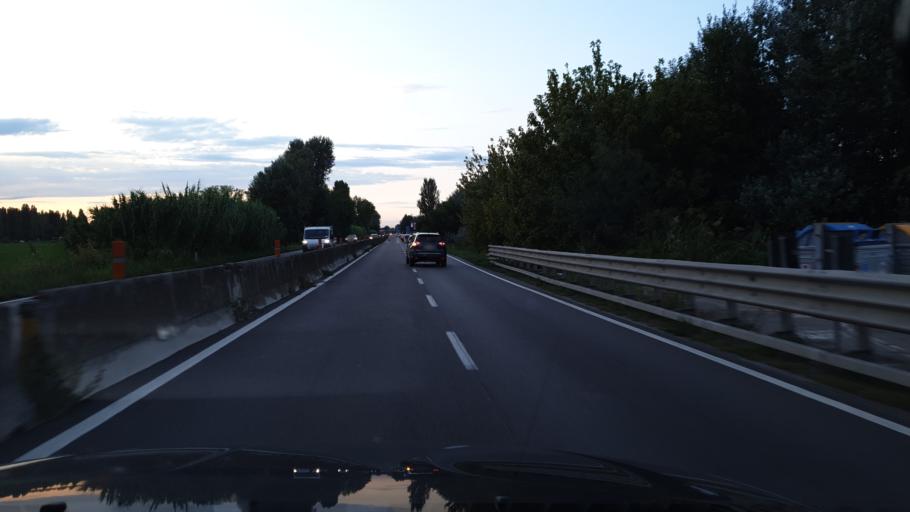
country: IT
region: Emilia-Romagna
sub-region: Provincia di Ravenna
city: Ravenna
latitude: 44.4044
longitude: 12.1772
